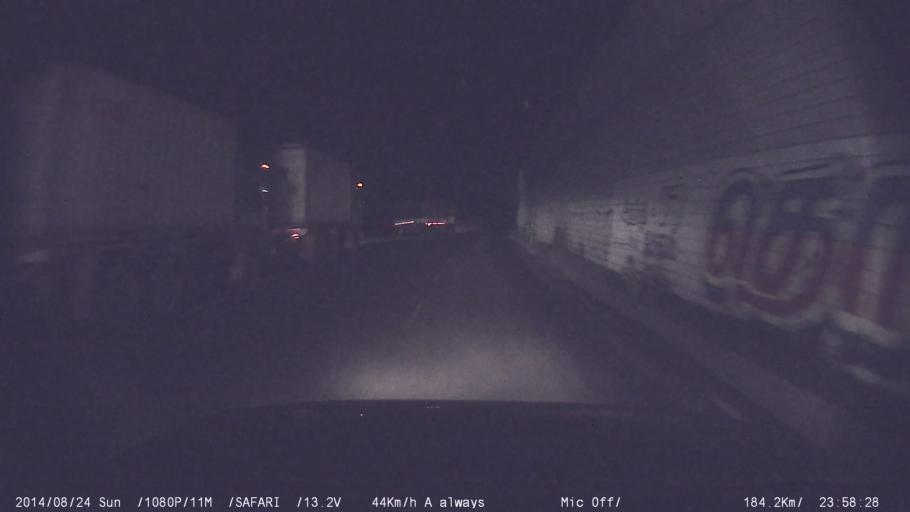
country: IN
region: Tamil Nadu
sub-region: Krishnagiri
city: Krishnagiri
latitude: 12.5058
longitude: 78.2232
